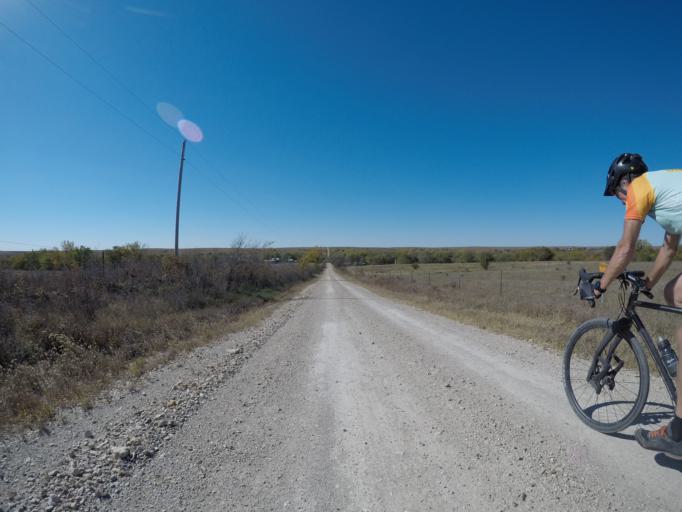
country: US
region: Kansas
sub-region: Wabaunsee County
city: Alma
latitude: 39.0290
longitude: -96.3841
